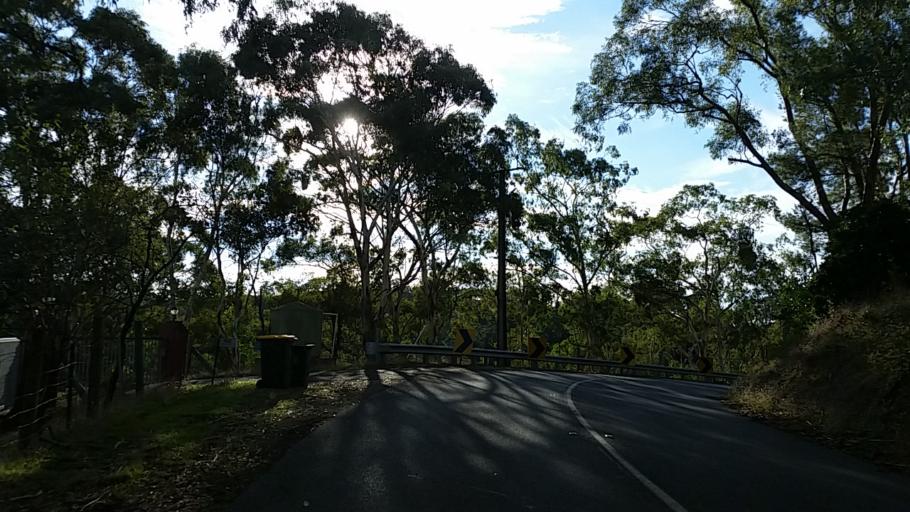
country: AU
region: South Australia
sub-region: Adelaide Hills
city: Adelaide Hills
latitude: -34.8899
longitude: 138.7492
